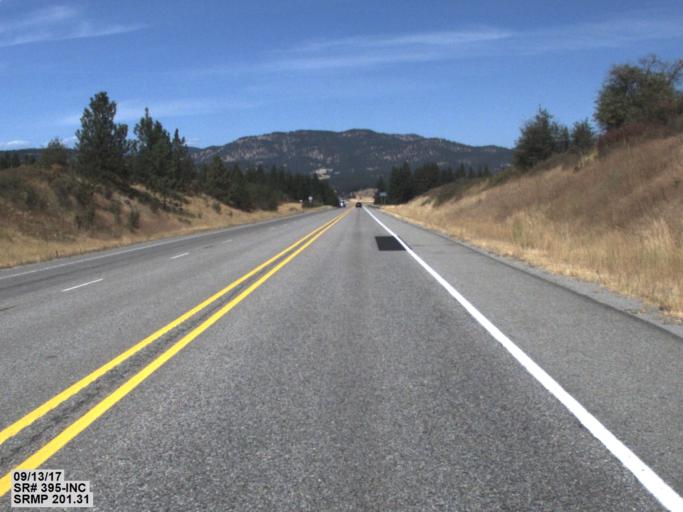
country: US
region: Washington
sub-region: Stevens County
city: Chewelah
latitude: 48.1943
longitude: -117.7040
